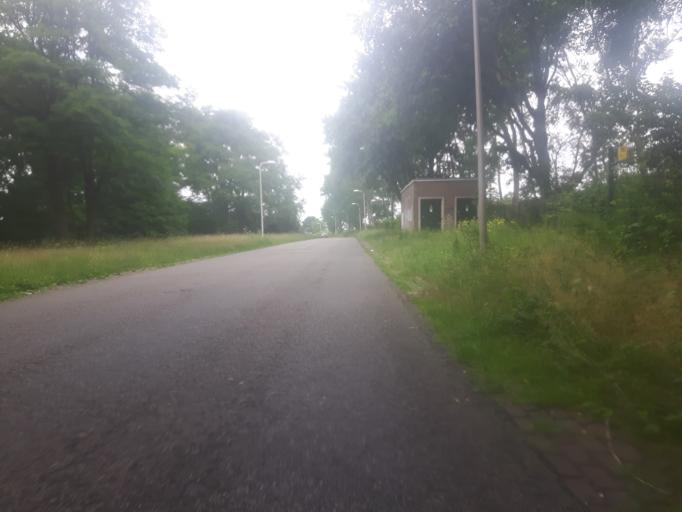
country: NL
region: Overijssel
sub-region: Gemeente Enschede
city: Enschede
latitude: 52.2246
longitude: 6.8586
